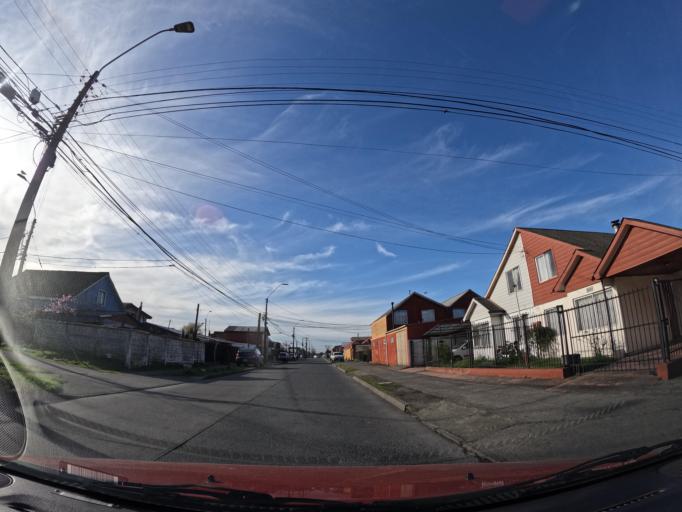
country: CL
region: Biobio
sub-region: Provincia de Concepcion
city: Talcahuano
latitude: -36.7489
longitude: -73.0866
